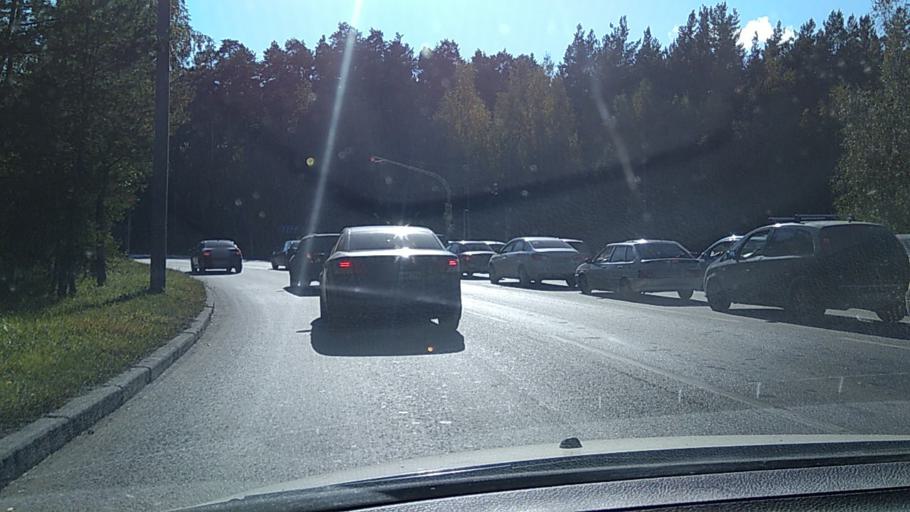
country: RU
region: Sverdlovsk
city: Sovkhoznyy
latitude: 56.8049
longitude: 60.5376
